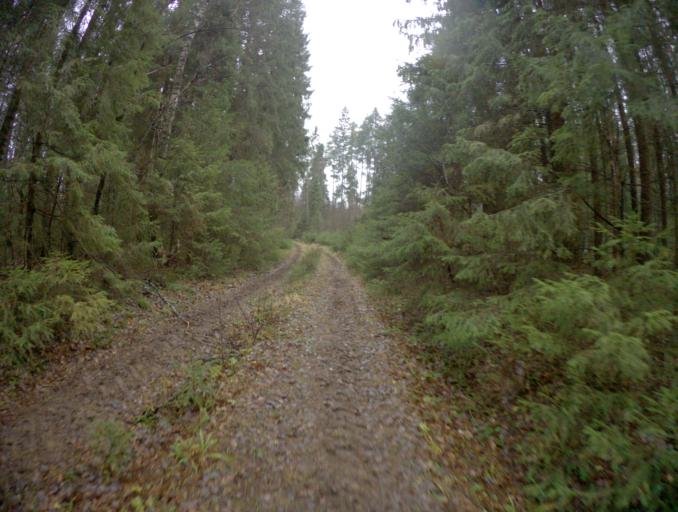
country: RU
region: Vladimir
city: Golovino
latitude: 56.0036
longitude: 40.4721
